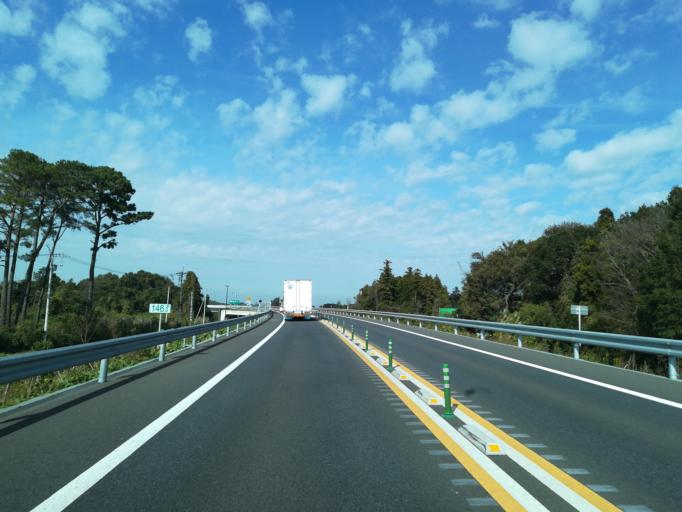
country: JP
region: Ibaraki
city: Ishige
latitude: 36.0756
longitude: 140.0128
